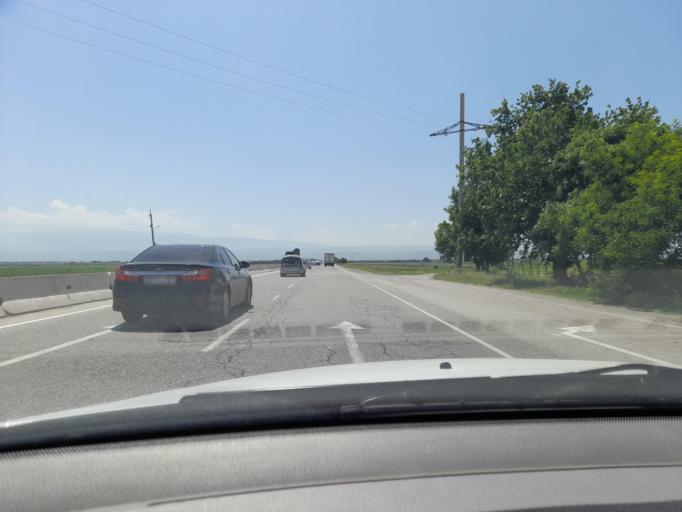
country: UZ
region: Jizzax
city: Jizzax
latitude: 40.1250
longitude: 67.9509
